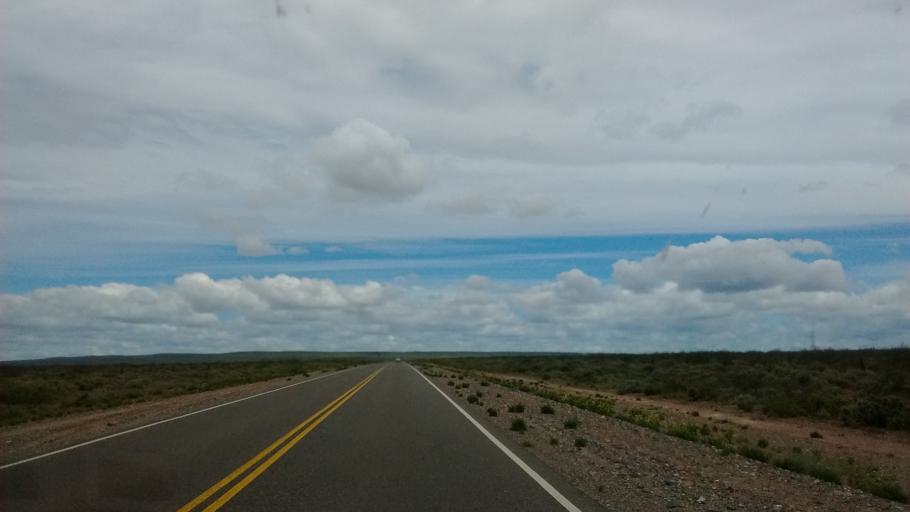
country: AR
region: Neuquen
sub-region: Departamento de Picun Leufu
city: Picun Leufu
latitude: -39.7067
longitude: -69.5052
